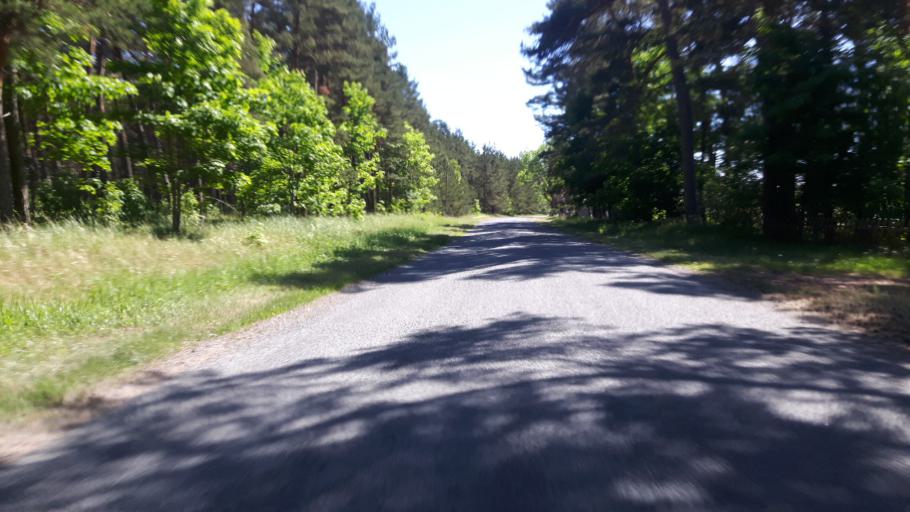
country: LV
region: Salacgrivas
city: Ainazi
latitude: 57.9347
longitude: 24.3918
